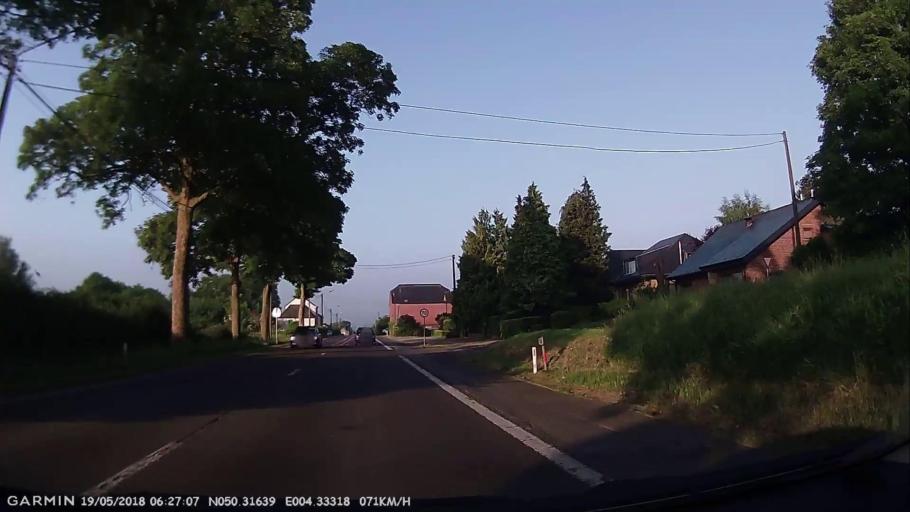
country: BE
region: Wallonia
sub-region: Province du Hainaut
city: Thuin
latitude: 50.3163
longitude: 4.3331
